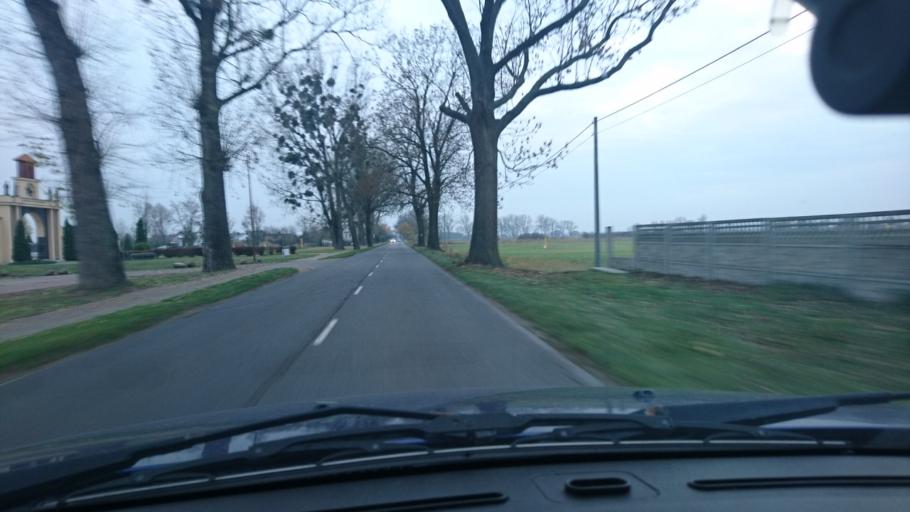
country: PL
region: Greater Poland Voivodeship
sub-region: Powiat ostrowski
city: Odolanow
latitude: 51.5713
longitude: 17.6670
